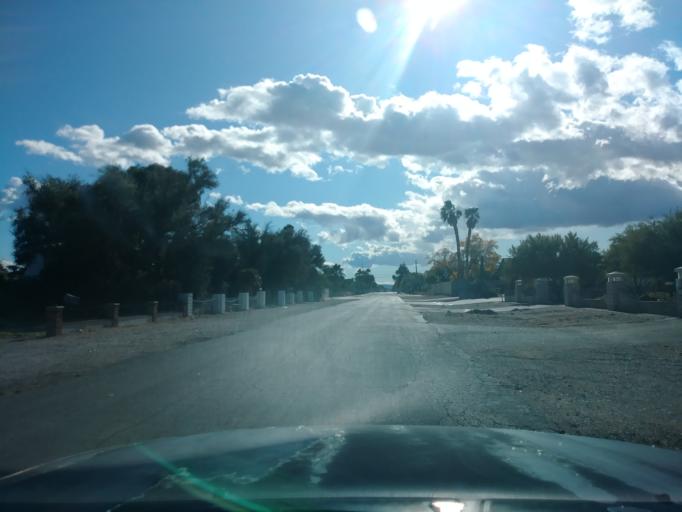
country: US
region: Nevada
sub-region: Clark County
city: Spring Valley
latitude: 36.1478
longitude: -115.2211
